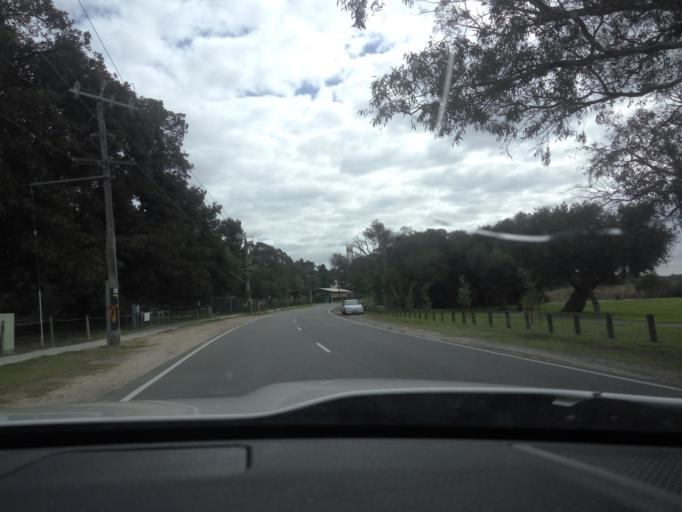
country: AU
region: Western Australia
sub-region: City of Cockburn
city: Bibra Lake
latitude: -32.0983
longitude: 115.8205
